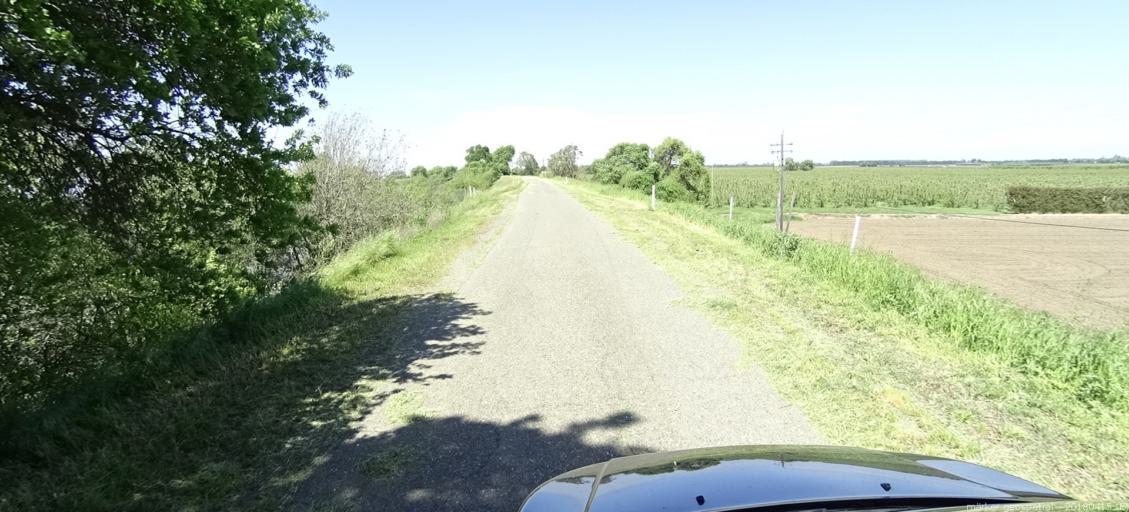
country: US
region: California
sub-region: Sacramento County
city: Walnut Grove
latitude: 38.2798
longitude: -121.6004
